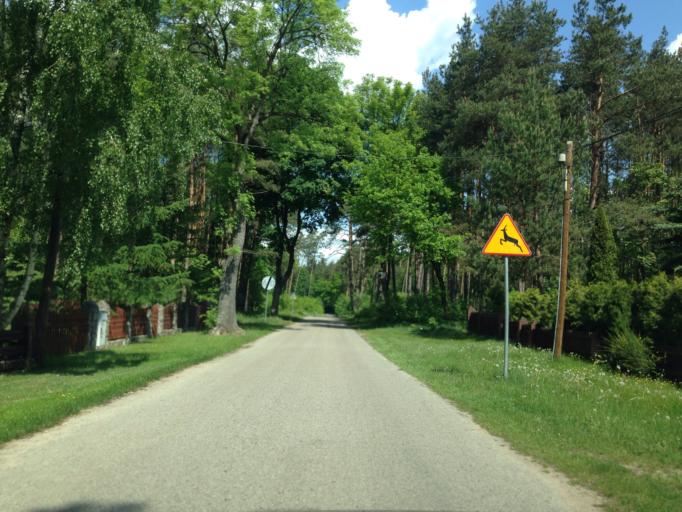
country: PL
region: Kujawsko-Pomorskie
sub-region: Powiat brodnicki
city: Brodnica
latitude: 53.3416
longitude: 19.3532
